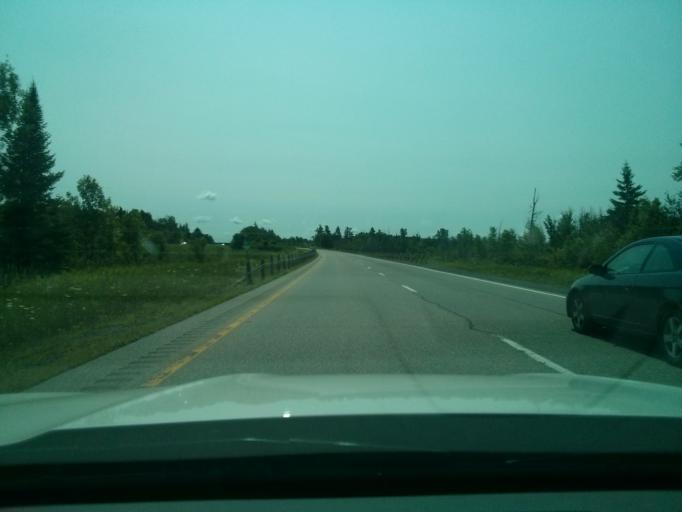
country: CA
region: Ontario
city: Prescott
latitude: 44.8765
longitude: -75.5613
